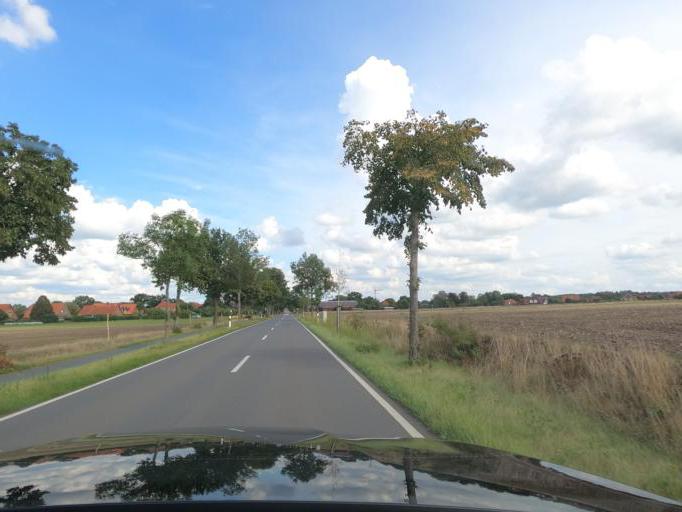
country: DE
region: Lower Saxony
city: Isernhagen Farster Bauerschaft
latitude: 52.5050
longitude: 9.8752
